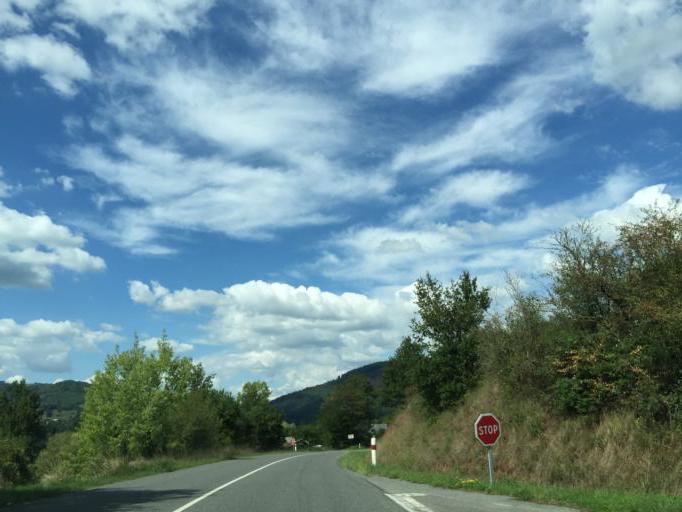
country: FR
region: Midi-Pyrenees
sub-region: Departement de l'Aveyron
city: Saint-Christophe-Vallon
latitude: 44.5377
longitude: 2.4082
